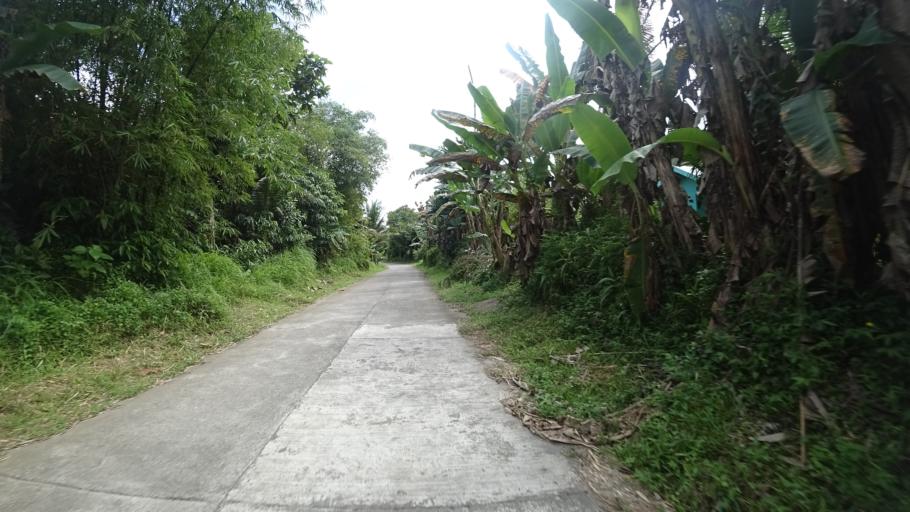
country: PH
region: Eastern Visayas
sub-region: Province of Leyte
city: Pastrana
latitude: 11.1667
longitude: 124.8695
